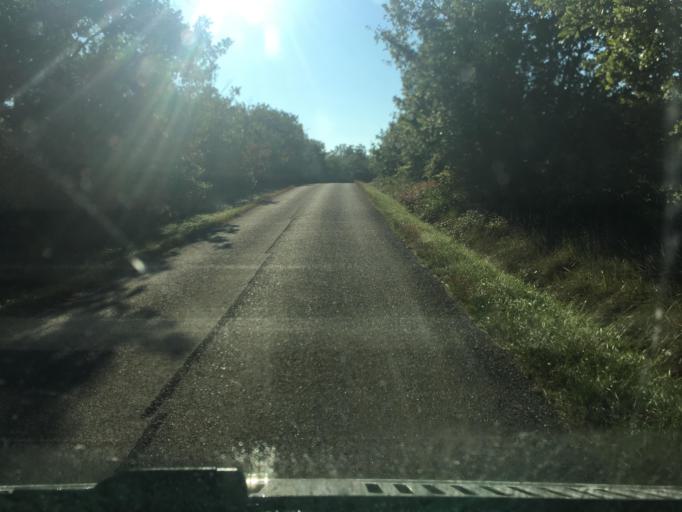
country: FR
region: Languedoc-Roussillon
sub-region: Departement du Gard
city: Goudargues
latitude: 44.1759
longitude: 4.3409
